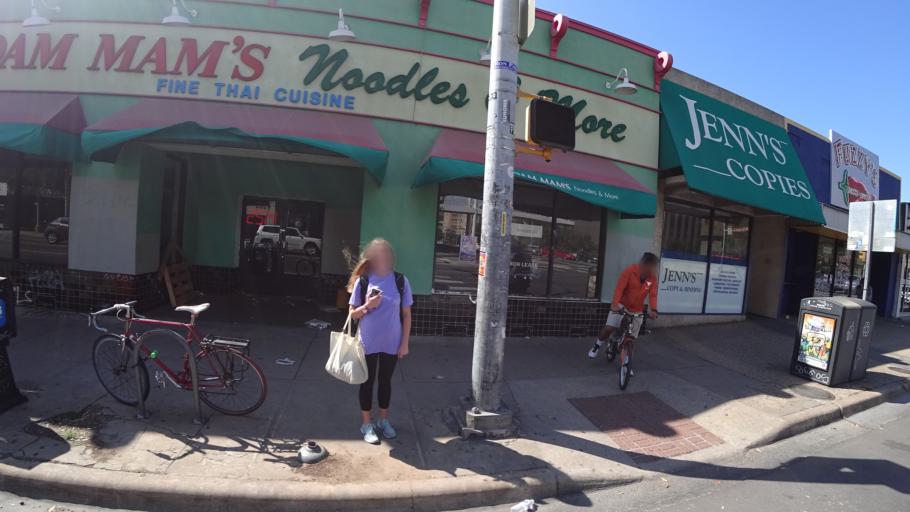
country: US
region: Texas
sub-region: Travis County
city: Austin
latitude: 30.2896
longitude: -97.7415
